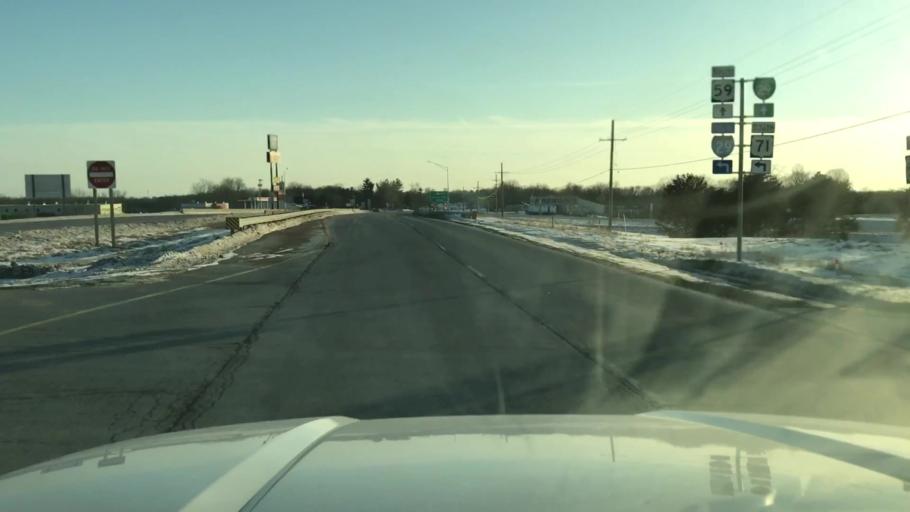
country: US
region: Missouri
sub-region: Andrew County
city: Country Club Village
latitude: 39.8595
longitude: -94.8104
